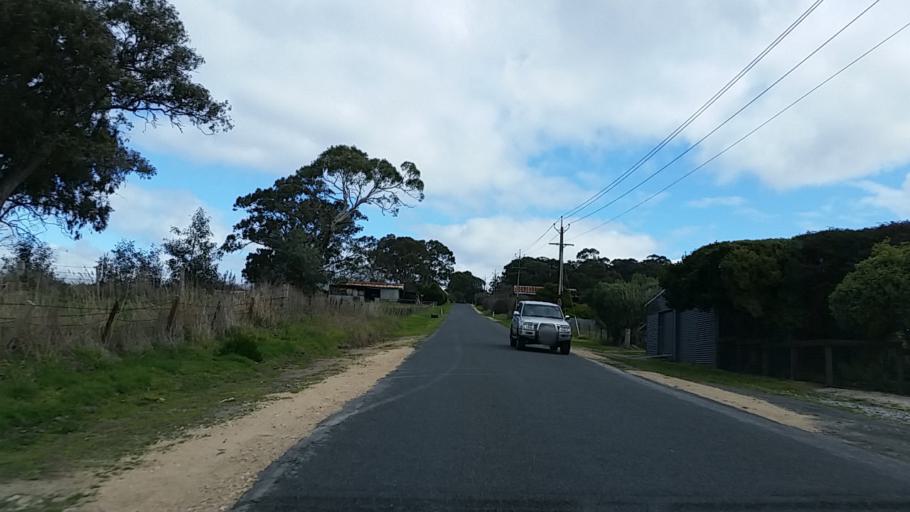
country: AU
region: South Australia
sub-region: Mount Barker
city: Little Hampton
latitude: -35.0668
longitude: 138.8479
